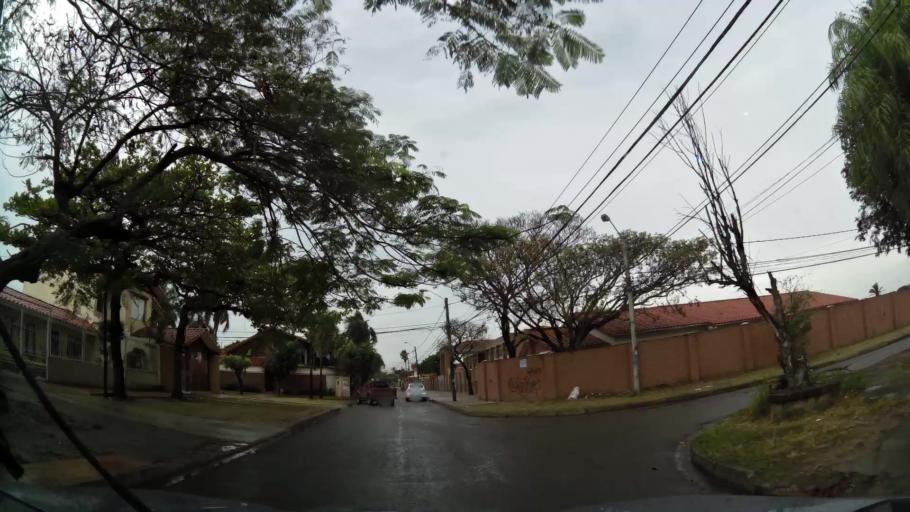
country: BO
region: Santa Cruz
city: Santa Cruz de la Sierra
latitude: -17.7702
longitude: -63.1517
